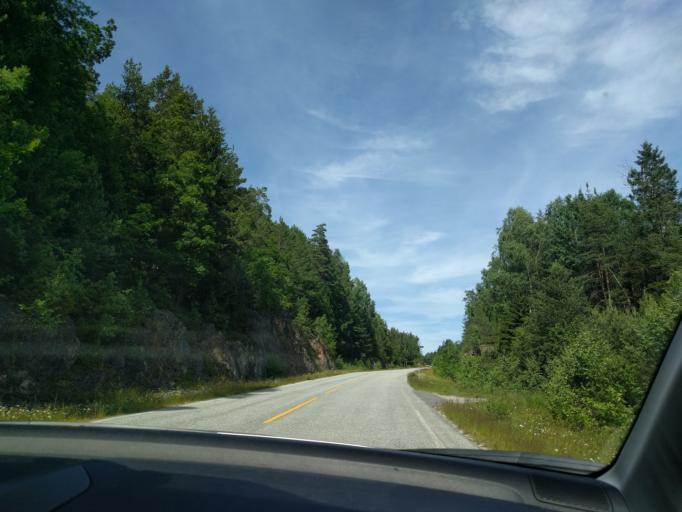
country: NO
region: Aust-Agder
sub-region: Gjerstad
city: Gjerstad
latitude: 58.8555
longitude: 9.1271
